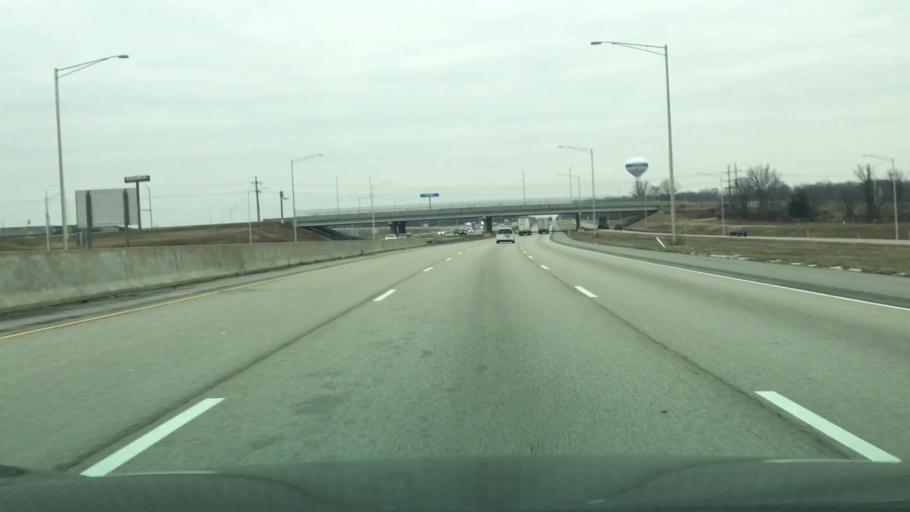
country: US
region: Illinois
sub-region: Williamson County
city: Marion
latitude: 37.7424
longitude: -88.9575
